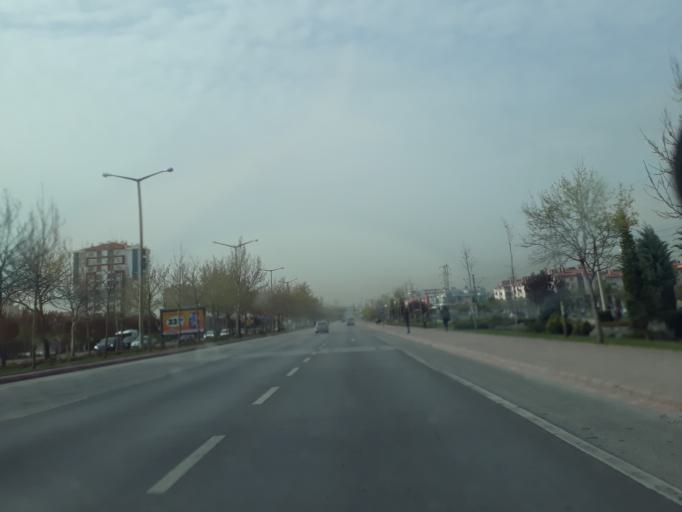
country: TR
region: Konya
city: Asagipinarbasi
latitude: 37.9829
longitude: 32.5172
